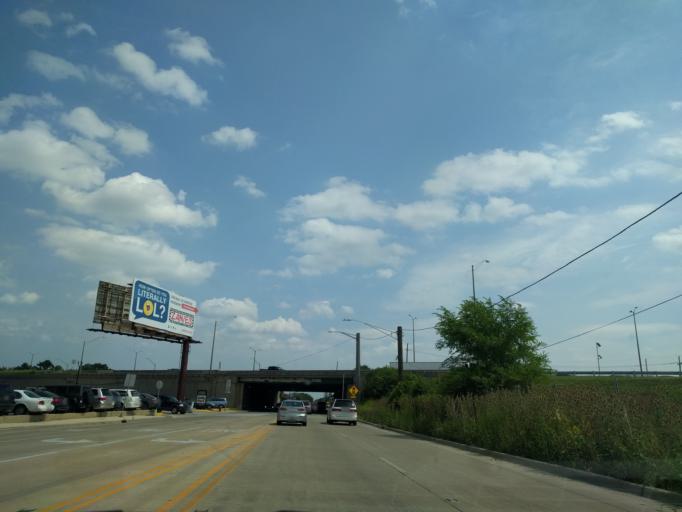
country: US
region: Illinois
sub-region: Cook County
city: Schiller Park
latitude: 41.9656
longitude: -87.8757
